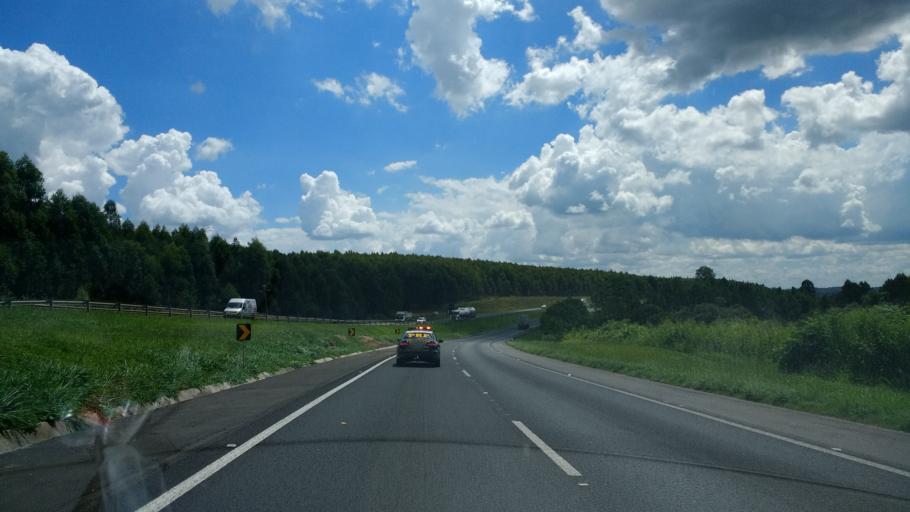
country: BR
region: Parana
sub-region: Palmeira
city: Palmeira
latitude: -25.2702
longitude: -49.9402
